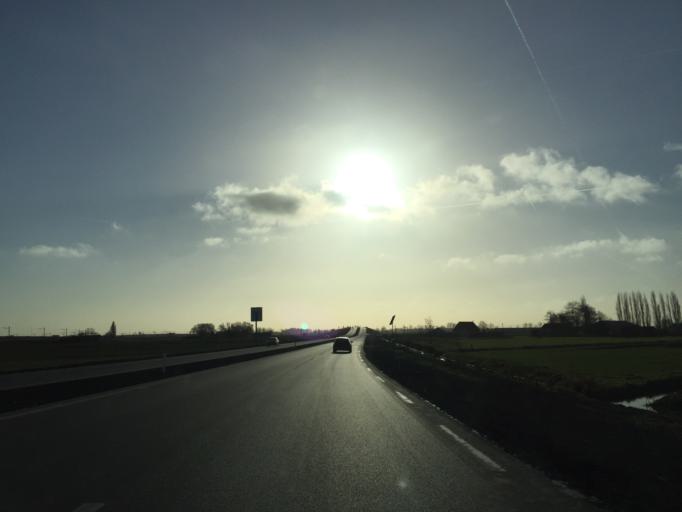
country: NL
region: South Holland
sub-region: Gemeente Waddinxveen
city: Waddinxveen
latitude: 52.0161
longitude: 4.6452
